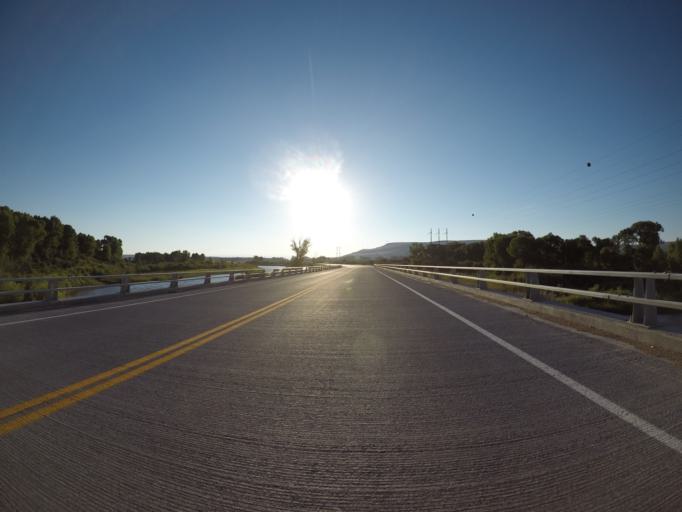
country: US
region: Wyoming
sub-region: Sublette County
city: Marbleton
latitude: 42.5702
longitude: -109.9509
